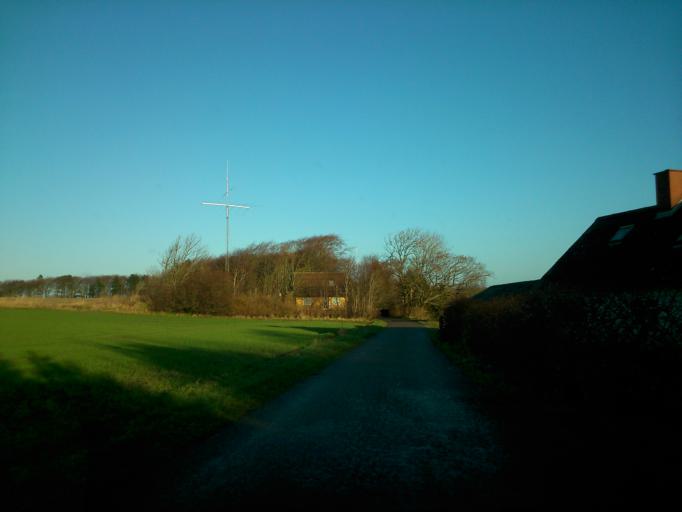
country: DK
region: Central Jutland
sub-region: Ringkobing-Skjern Kommune
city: Skjern
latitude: 55.9773
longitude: 8.5654
